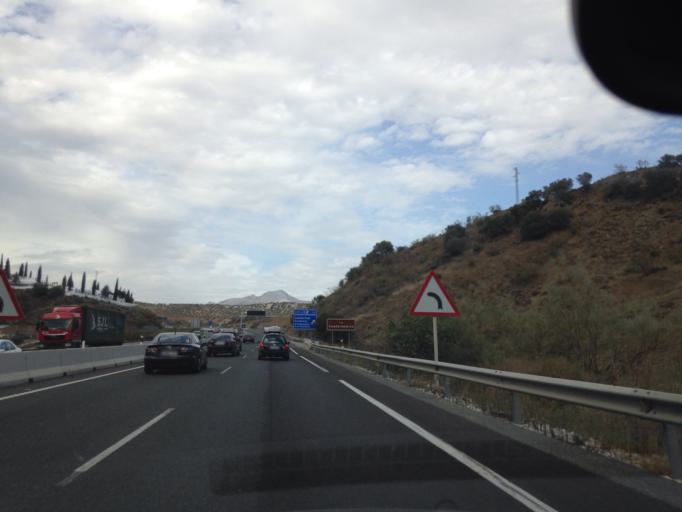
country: ES
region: Andalusia
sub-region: Provincia de Malaga
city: Casabermeja
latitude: 36.8926
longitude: -4.4218
